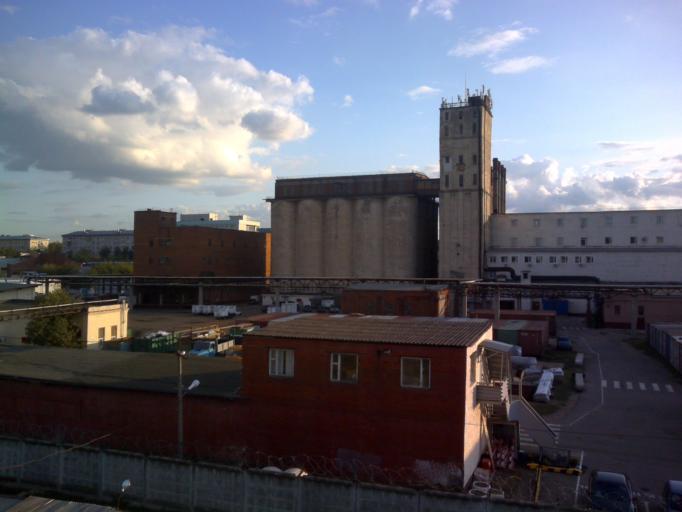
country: RU
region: Moscow
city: Ostankinskiy
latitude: 55.8213
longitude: 37.5964
